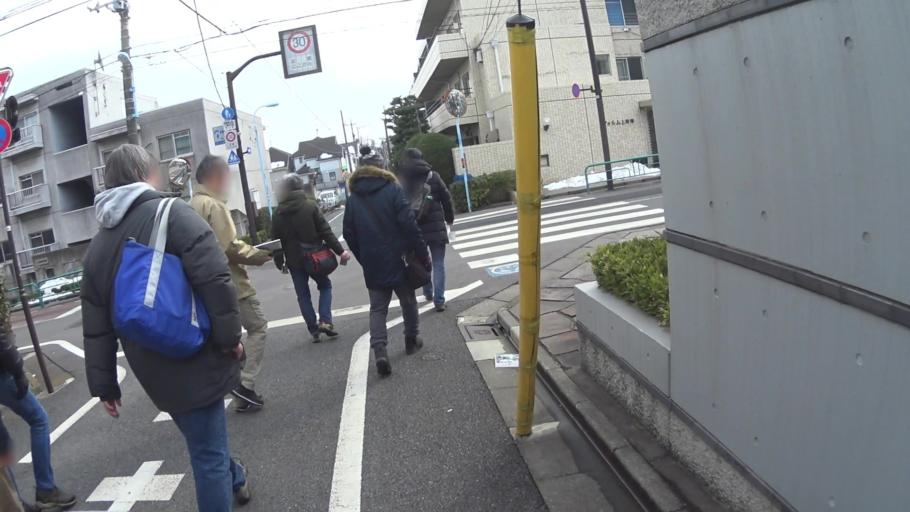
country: JP
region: Tokyo
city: Musashino
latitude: 35.7214
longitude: 139.6045
